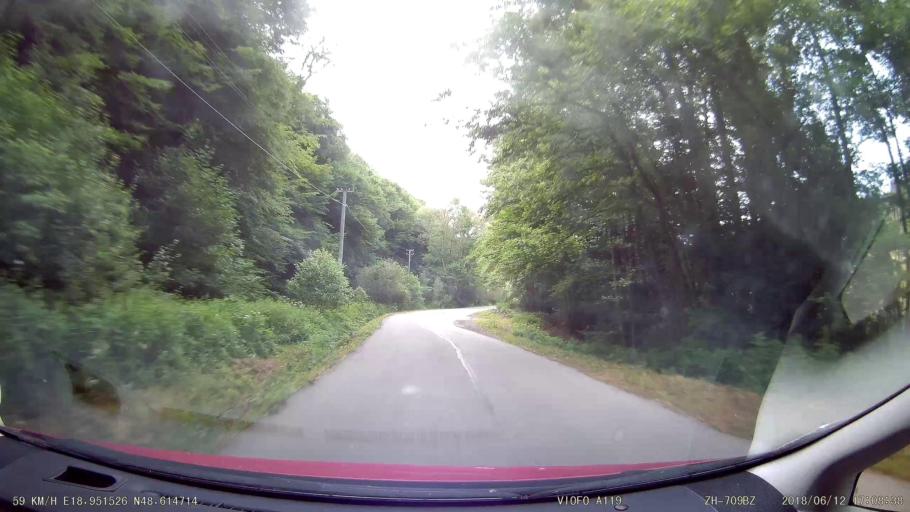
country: SK
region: Banskobystricky
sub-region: Okres Ziar nad Hronom
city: Kremnica
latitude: 48.6150
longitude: 18.9514
